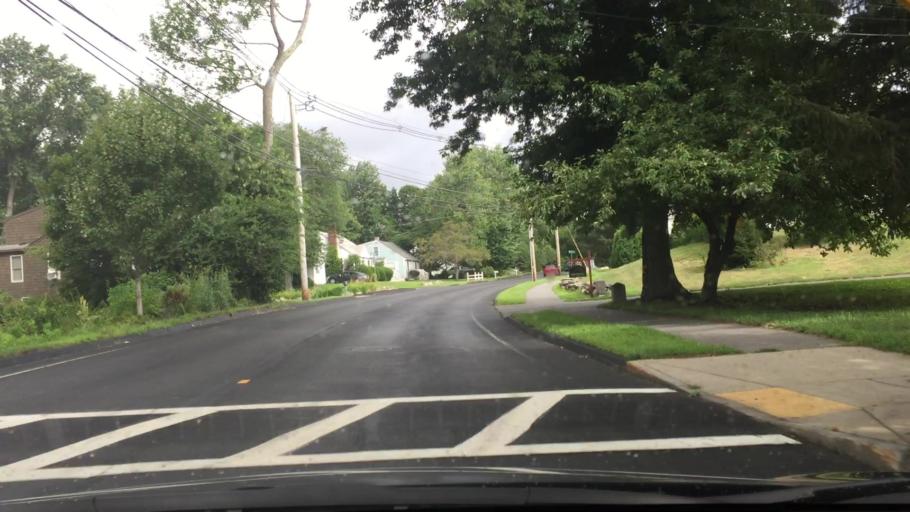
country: US
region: Massachusetts
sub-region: Middlesex County
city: Littleton Common
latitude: 42.5396
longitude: -71.4688
